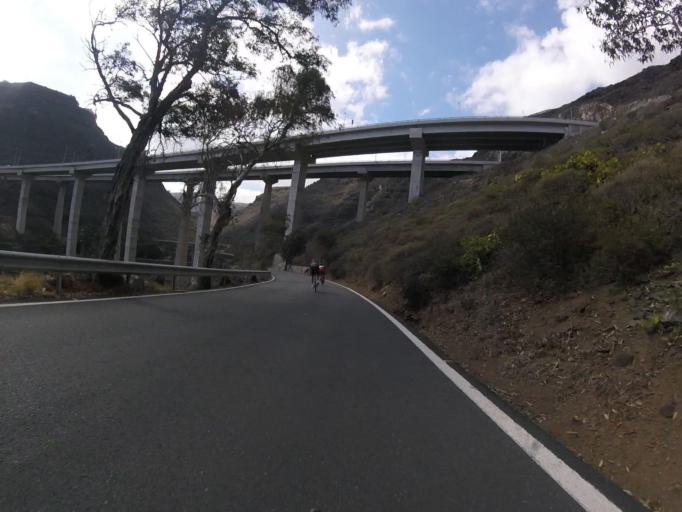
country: ES
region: Canary Islands
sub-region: Provincia de Las Palmas
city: Moya
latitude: 28.1402
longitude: -15.5913
